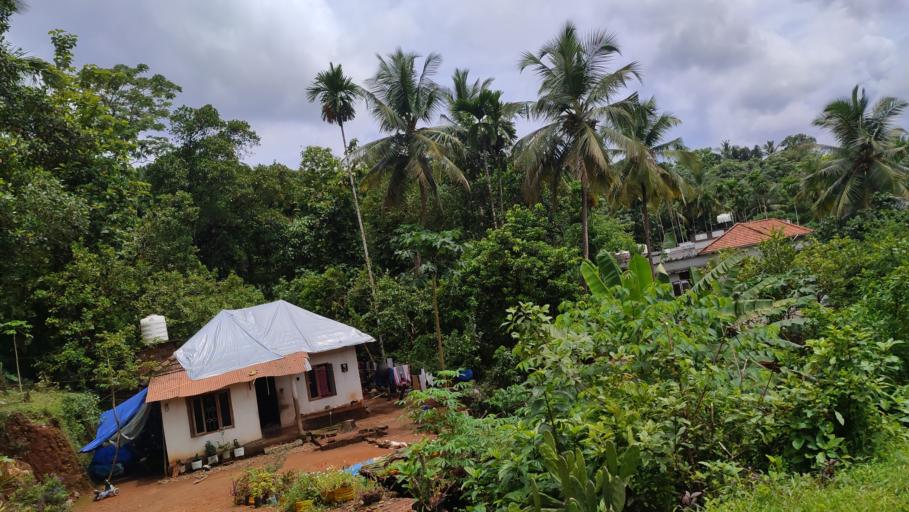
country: IN
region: Kerala
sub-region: Kasaragod District
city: Nileshwar
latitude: 12.2957
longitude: 75.2835
